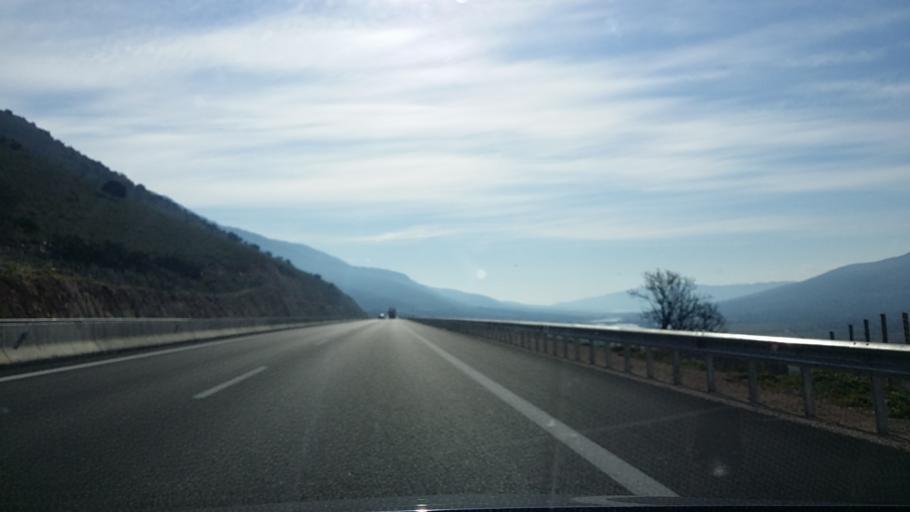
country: GR
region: West Greece
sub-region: Nomos Aitolias kai Akarnanias
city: Amfilochia
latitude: 38.8382
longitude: 21.1823
